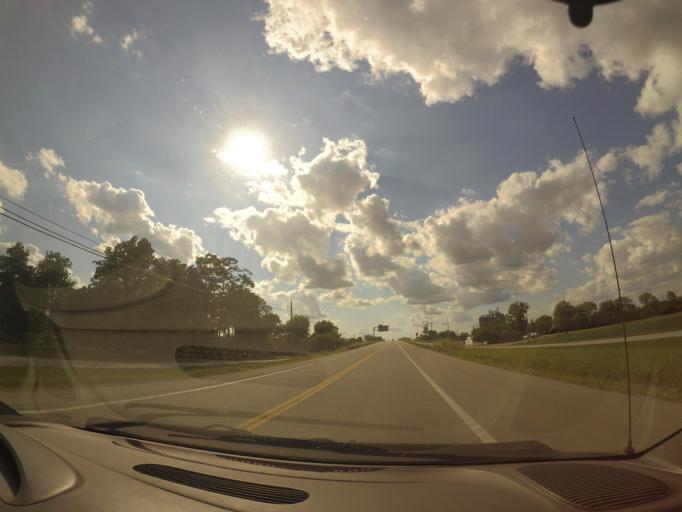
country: US
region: Ohio
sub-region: Wood County
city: Luckey
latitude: 41.4940
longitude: -83.4695
